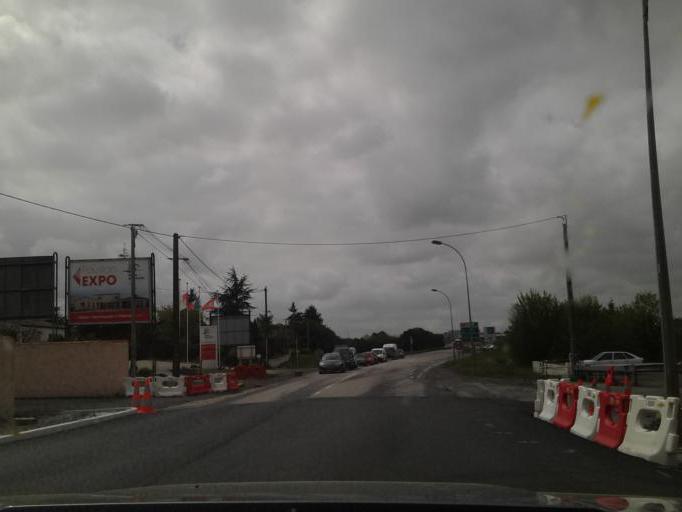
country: FR
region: Pays de la Loire
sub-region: Departement de la Vendee
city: Fontenay-le-Comte
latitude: 46.4500
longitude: -0.8095
